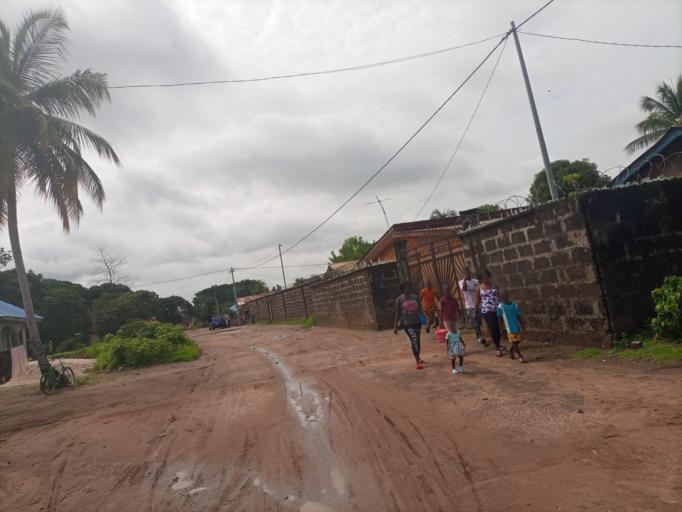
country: SL
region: Northern Province
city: Sawkta
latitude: 8.6246
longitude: -13.2062
